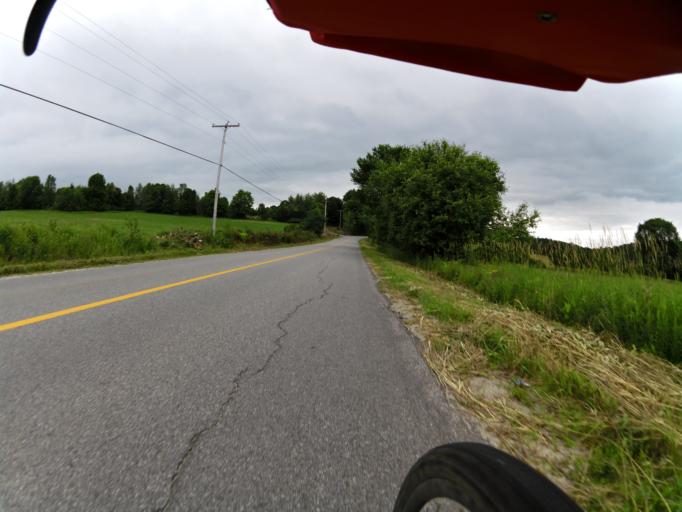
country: CA
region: Quebec
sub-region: Outaouais
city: Wakefield
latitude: 45.7226
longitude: -75.9695
